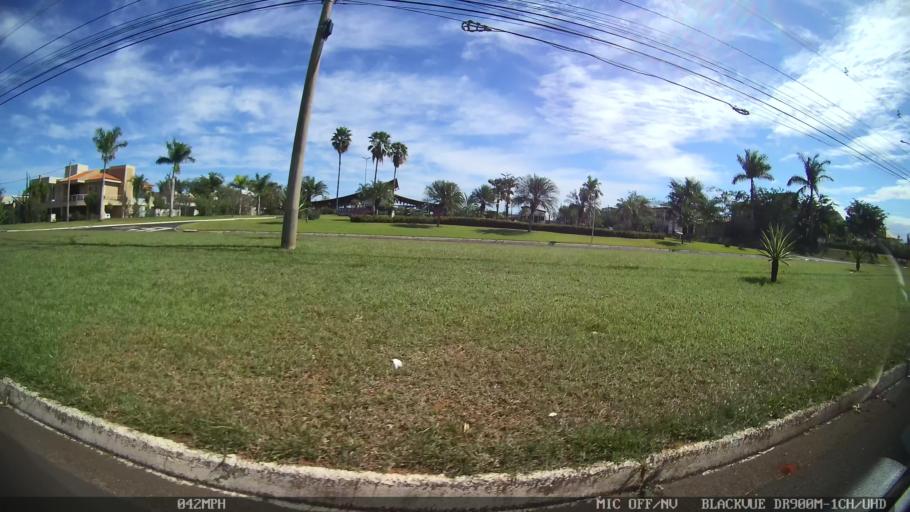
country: BR
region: Sao Paulo
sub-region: Sao Jose Do Rio Preto
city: Sao Jose do Rio Preto
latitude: -20.8220
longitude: -49.4816
